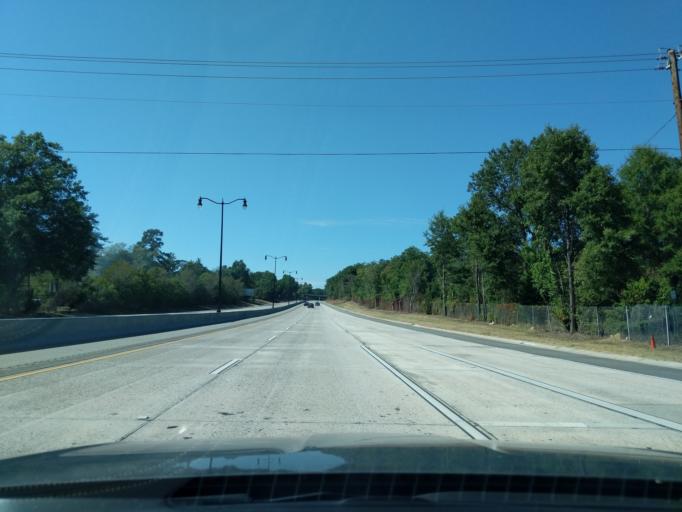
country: US
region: Georgia
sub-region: Richmond County
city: Augusta
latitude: 33.4847
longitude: -82.0001
